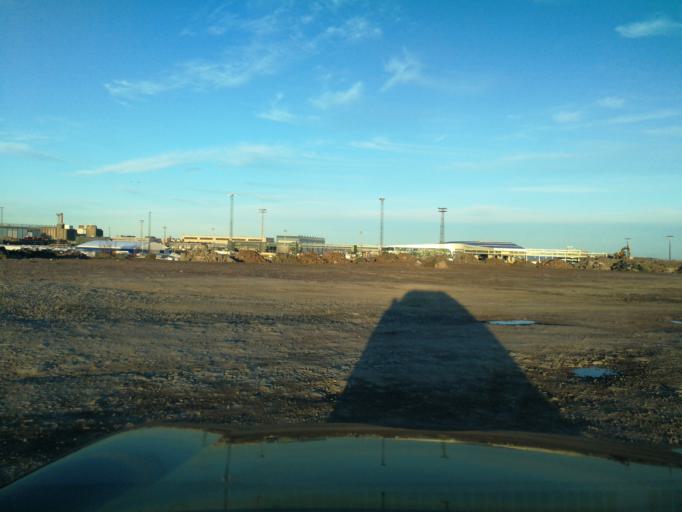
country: FI
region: Uusimaa
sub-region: Helsinki
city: Helsinki
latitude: 60.1522
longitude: 24.9044
